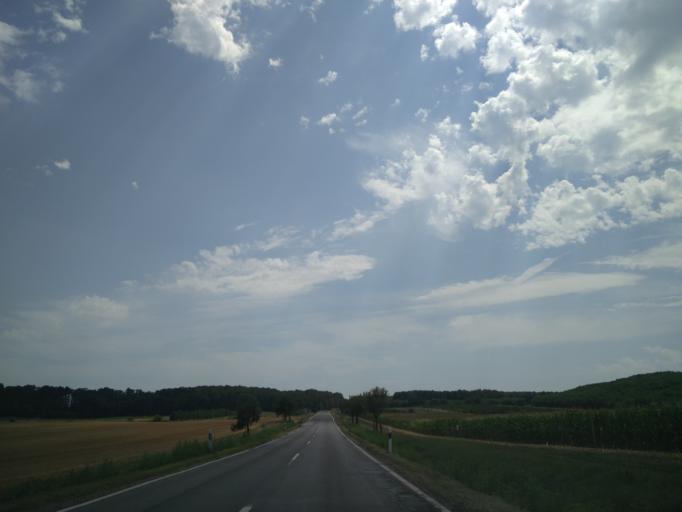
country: HU
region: Zala
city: Zalaegerszeg
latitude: 46.9192
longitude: 16.8590
